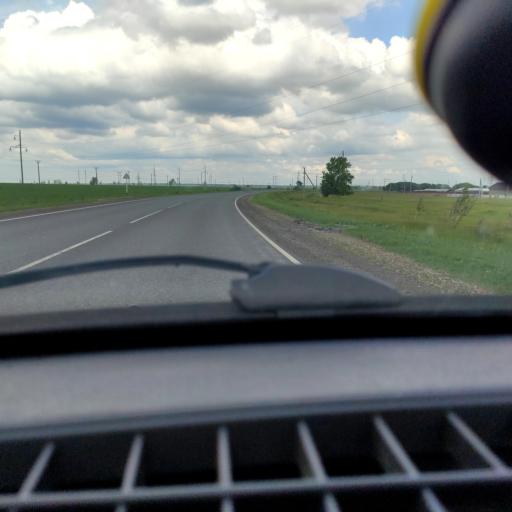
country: RU
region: Samara
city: Povolzhskiy
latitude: 53.6341
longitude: 49.6576
